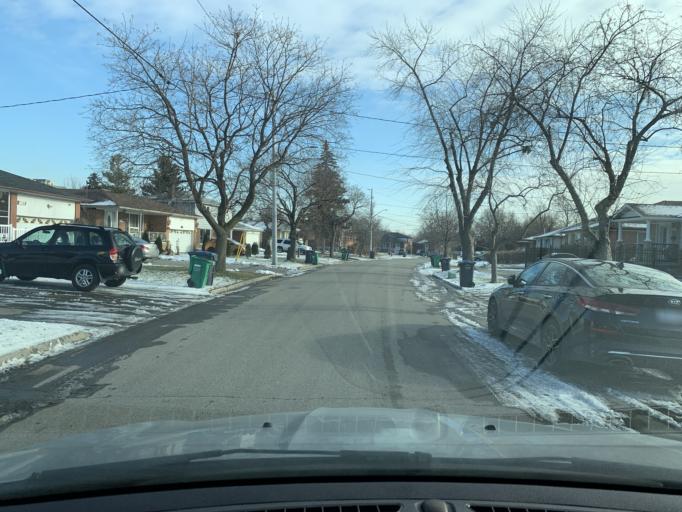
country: CA
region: Ontario
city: Etobicoke
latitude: 43.7236
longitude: -79.6285
